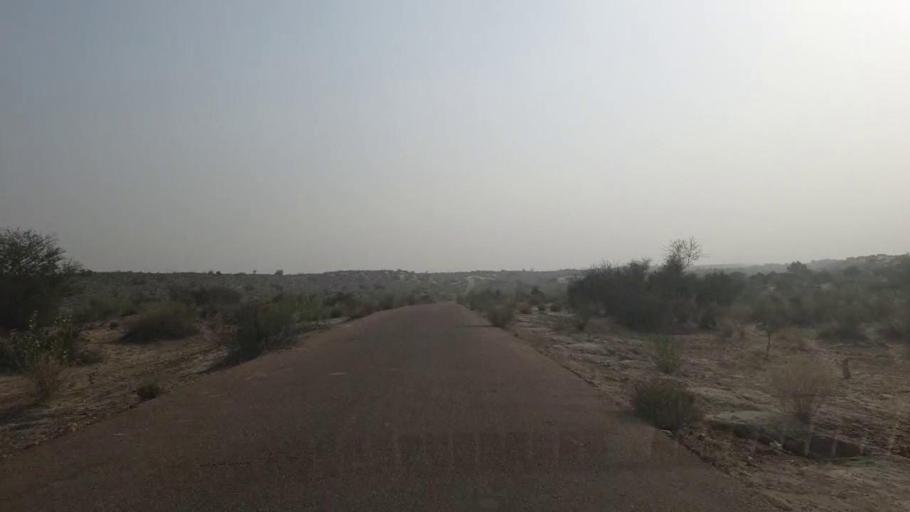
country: PK
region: Sindh
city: Chor
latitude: 25.4579
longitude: 69.9652
